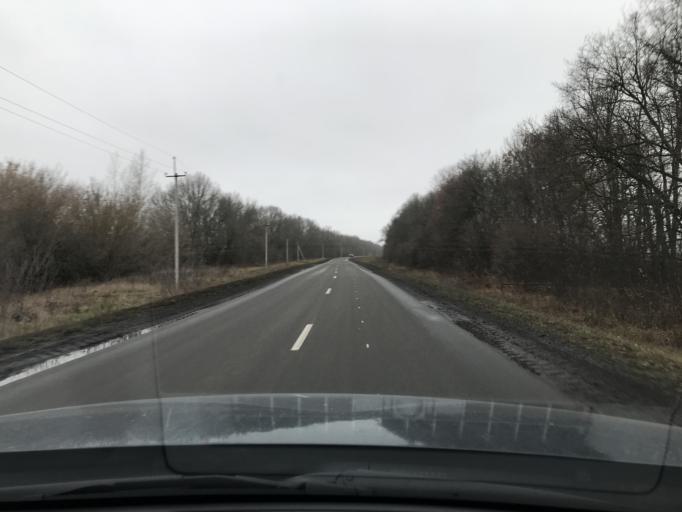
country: RU
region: Penza
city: Zemetchino
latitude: 53.5254
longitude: 42.6540
